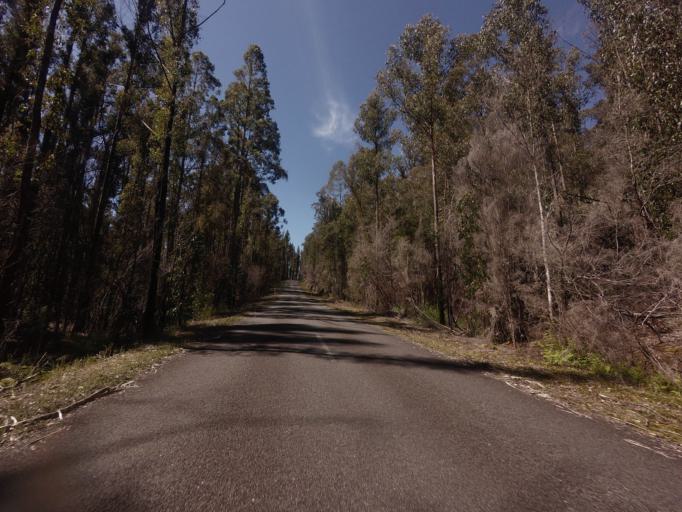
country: AU
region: Tasmania
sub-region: Huon Valley
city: Geeveston
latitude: -42.8424
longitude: 146.2526
